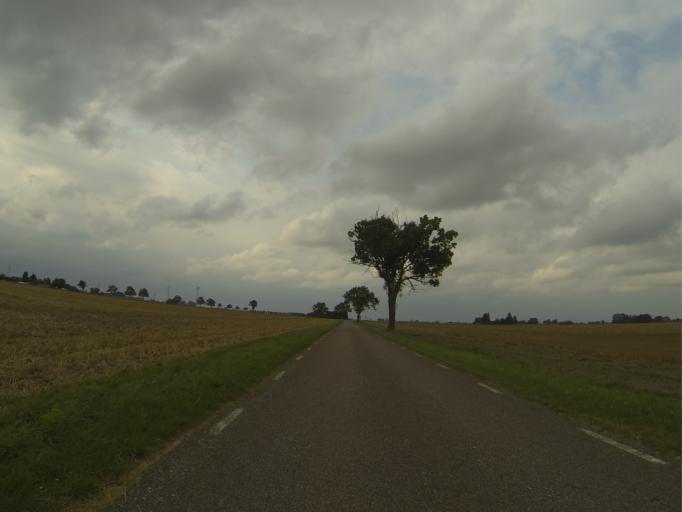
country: SE
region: Skane
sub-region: Kavlinge Kommun
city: Kaevlinge
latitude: 55.7621
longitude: 13.1557
